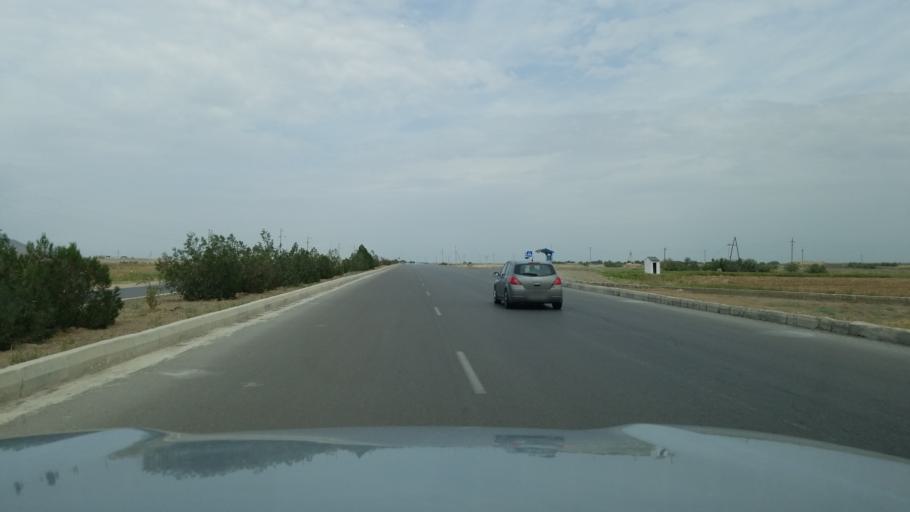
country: TM
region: Ahal
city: Arcabil
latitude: 38.2205
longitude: 57.8011
